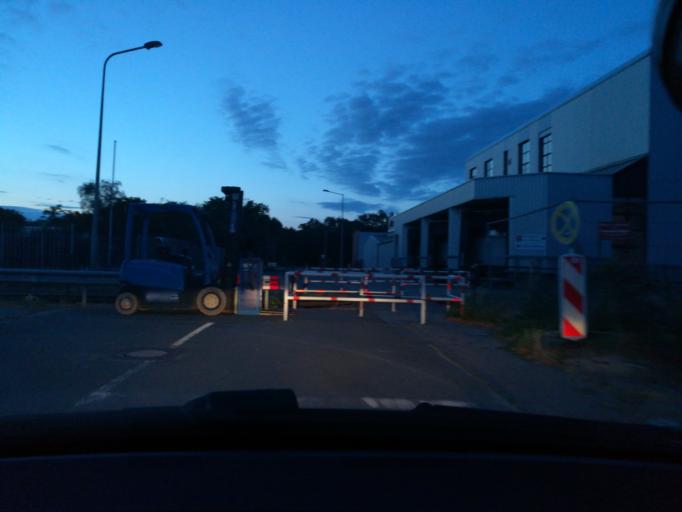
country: DE
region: North Rhine-Westphalia
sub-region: Regierungsbezirk Detmold
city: Minden
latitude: 52.2998
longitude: 8.9078
